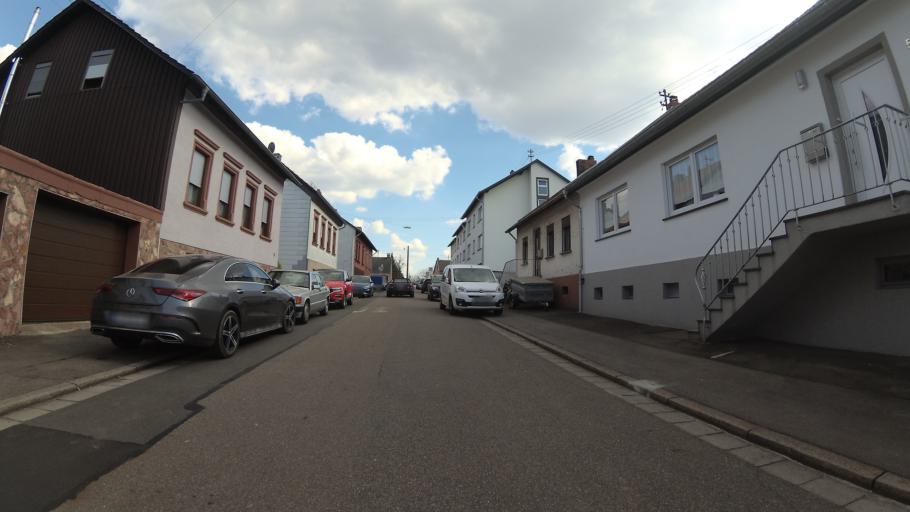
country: DE
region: Saarland
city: Riegelsberg
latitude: 49.2945
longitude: 6.9304
